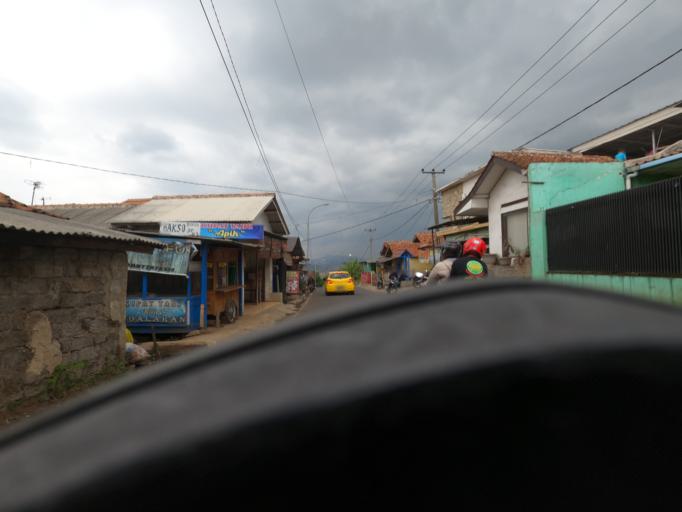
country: ID
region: West Java
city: Padalarang
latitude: -6.8398
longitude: 107.5063
